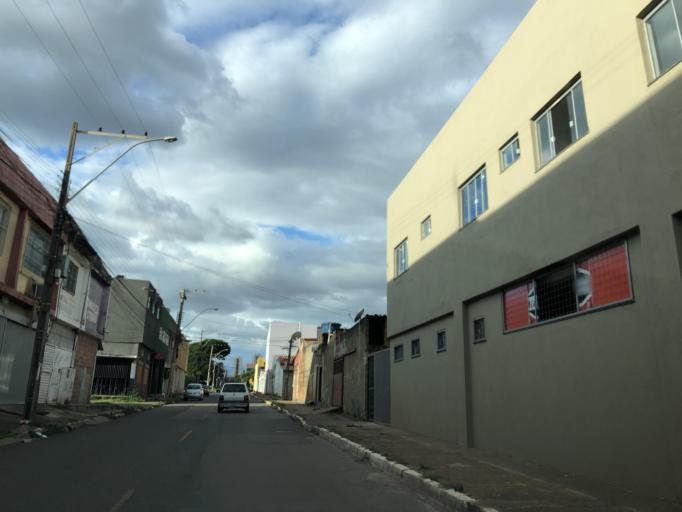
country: BR
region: Goias
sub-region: Luziania
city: Luziania
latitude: -16.0287
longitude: -48.0602
